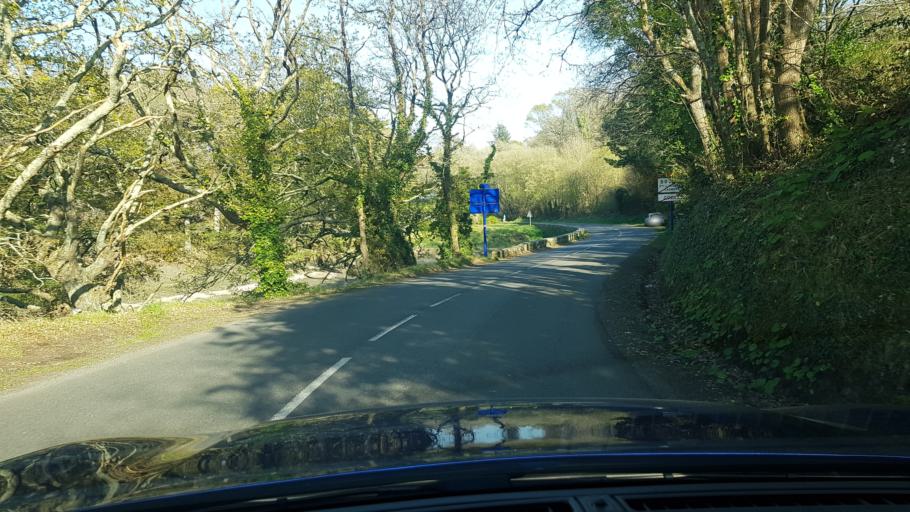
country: FR
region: Brittany
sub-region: Departement du Finistere
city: Clohars-Carnoet
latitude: 47.7765
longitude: -3.6035
